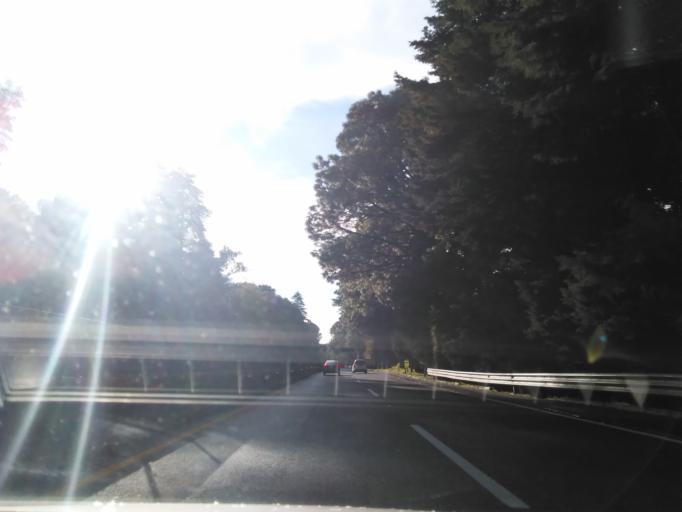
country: MX
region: Morelos
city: Tres Marias
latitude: 19.0442
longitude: -99.2343
